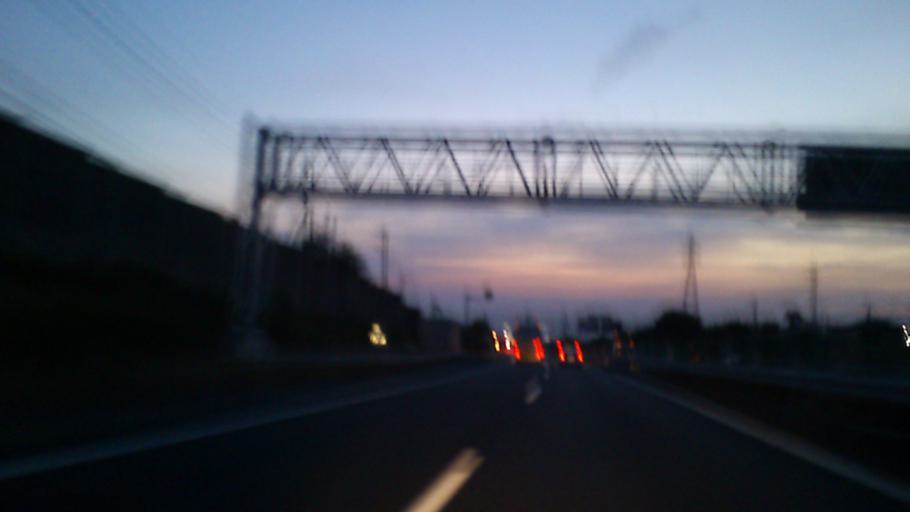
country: JP
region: Aichi
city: Kasugai
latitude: 35.2901
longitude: 136.9624
